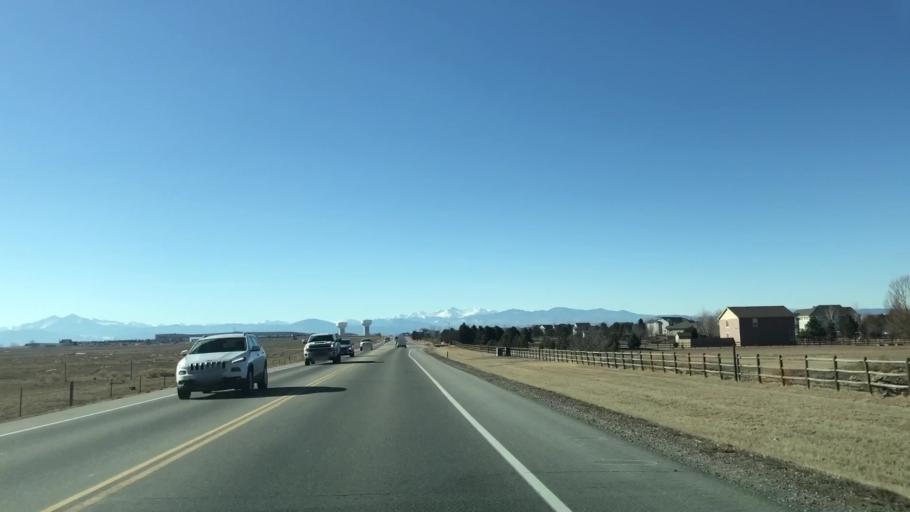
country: US
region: Colorado
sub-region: Weld County
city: Windsor
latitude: 40.4359
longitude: -104.9480
